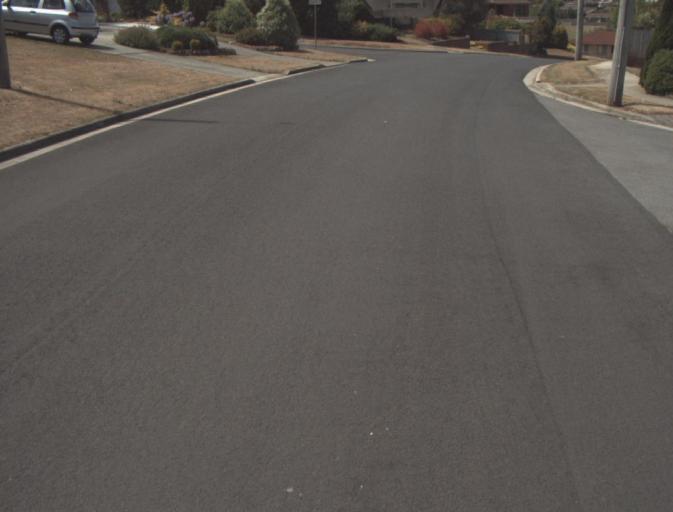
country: AU
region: Tasmania
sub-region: Launceston
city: Mayfield
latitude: -41.3811
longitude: 147.1188
